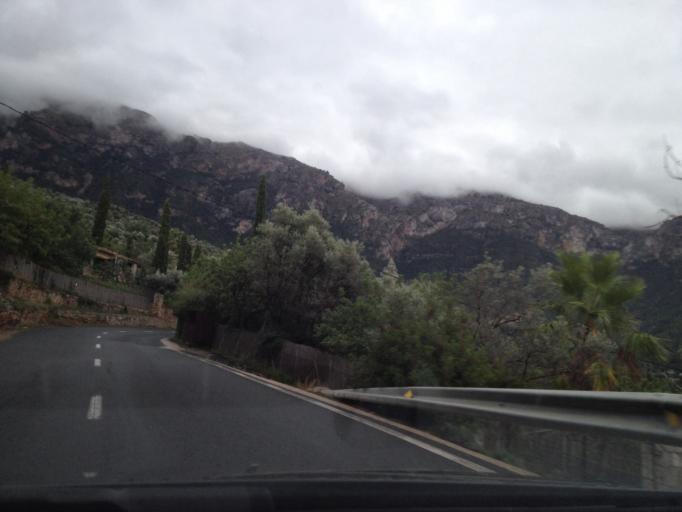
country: ES
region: Balearic Islands
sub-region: Illes Balears
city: Deia
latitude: 39.7562
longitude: 2.6467
